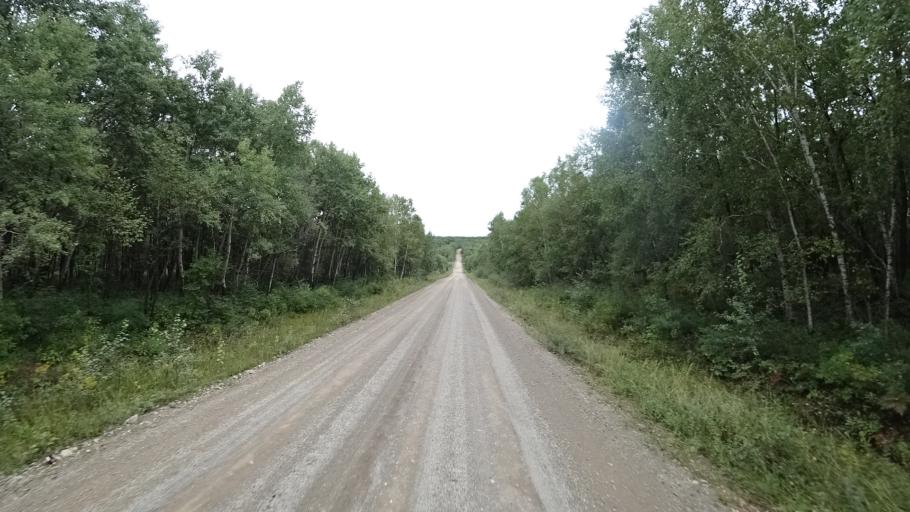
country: RU
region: Primorskiy
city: Ivanovka
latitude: 44.0308
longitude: 132.5083
